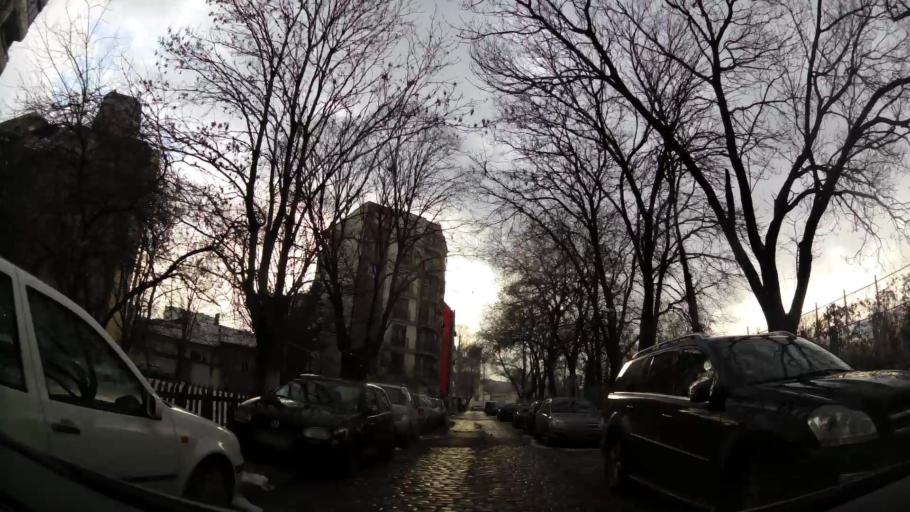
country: BG
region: Sofia-Capital
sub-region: Stolichna Obshtina
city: Sofia
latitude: 42.6987
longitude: 23.2942
